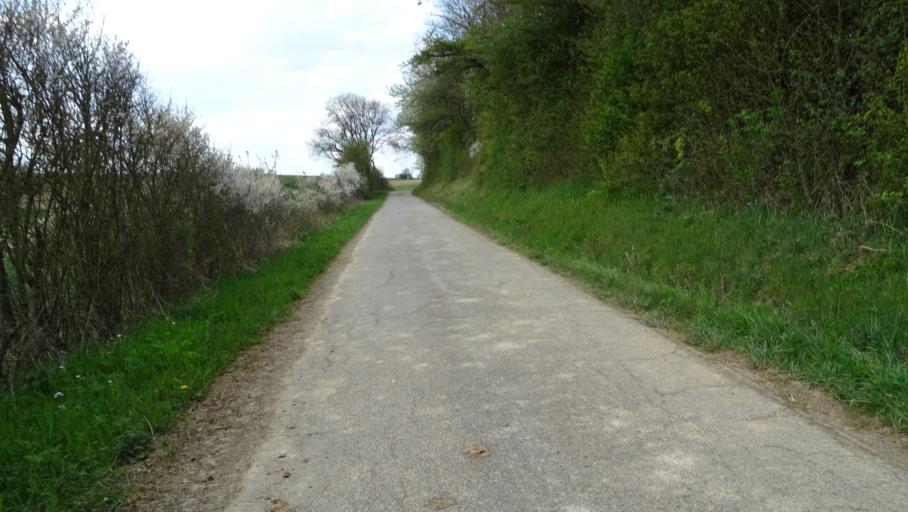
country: DE
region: Baden-Wuerttemberg
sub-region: Karlsruhe Region
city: Billigheim
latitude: 49.3848
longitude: 9.2503
